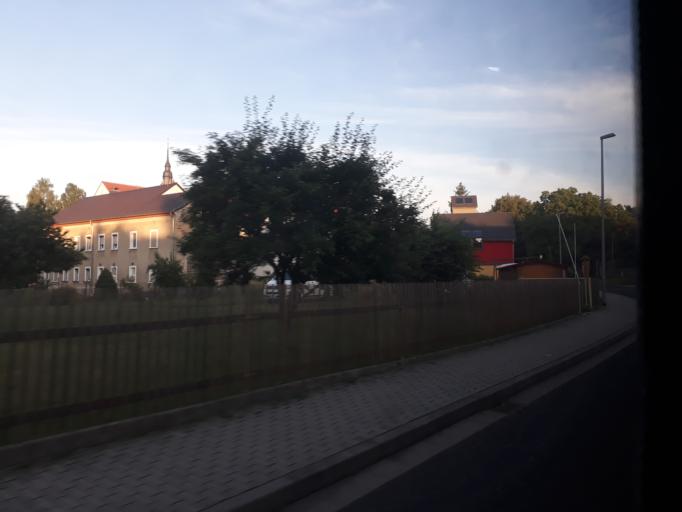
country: DE
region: Saxony
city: Radeberg
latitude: 51.0602
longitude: 13.8841
